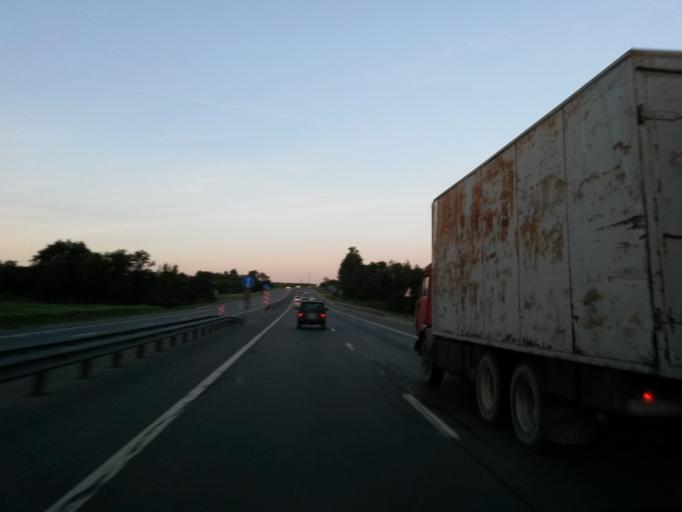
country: RU
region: Moskovskaya
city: Sergiyev Posad
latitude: 56.2796
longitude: 38.2039
